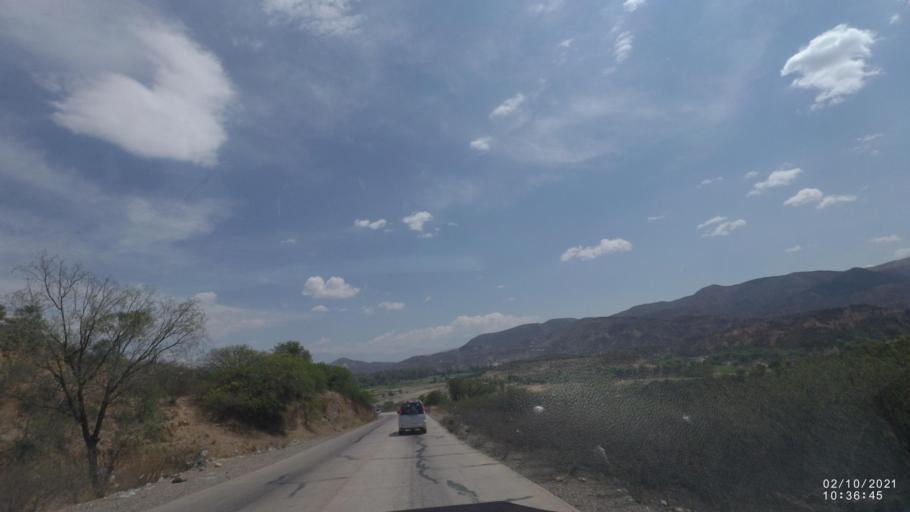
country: BO
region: Cochabamba
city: Capinota
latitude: -17.6471
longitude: -66.2588
